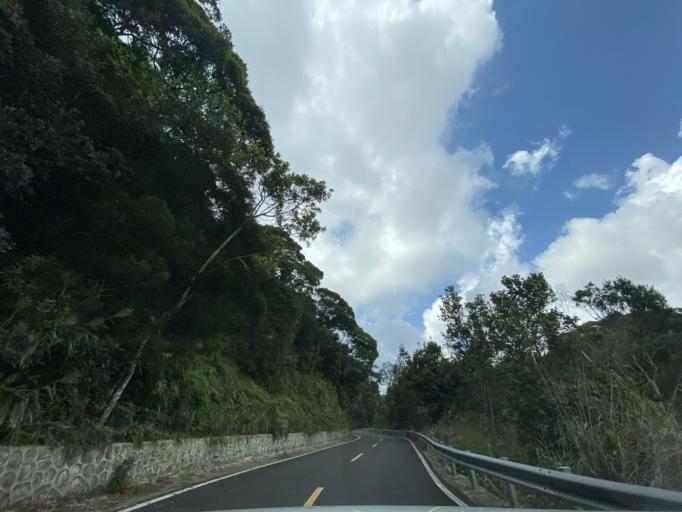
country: CN
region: Hainan
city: Diaoluoshan
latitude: 18.7208
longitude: 109.8753
